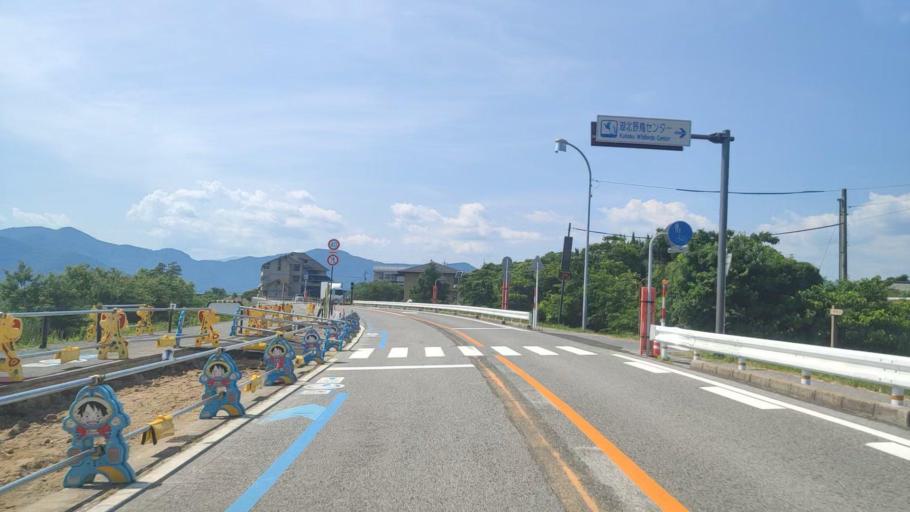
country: JP
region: Shiga Prefecture
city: Nagahama
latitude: 35.4466
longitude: 136.1894
